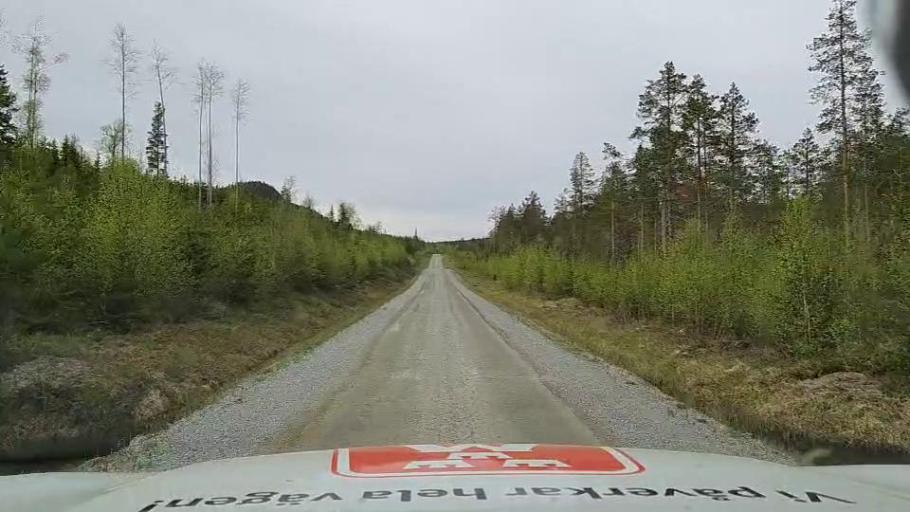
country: SE
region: Jaemtland
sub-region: Bergs Kommun
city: Hoverberg
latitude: 62.5521
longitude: 14.8975
